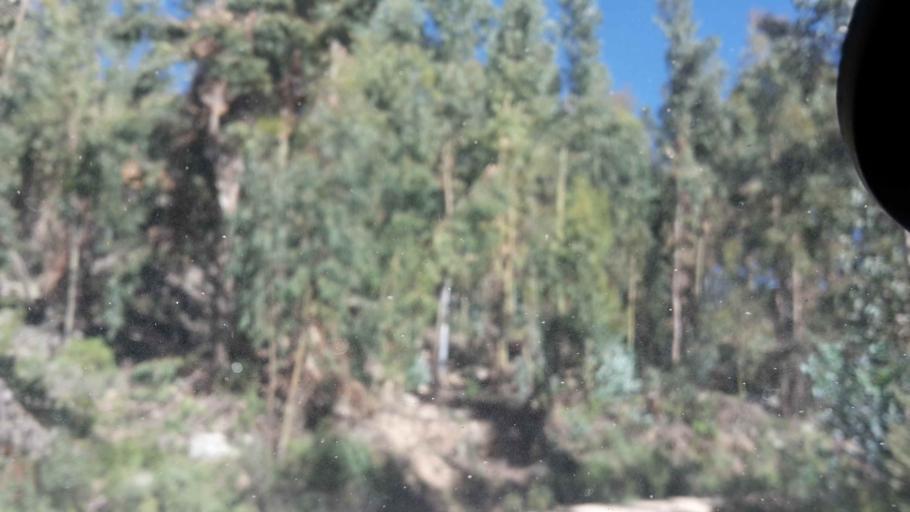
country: BO
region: Cochabamba
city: Arani
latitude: -17.6728
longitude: -65.7286
